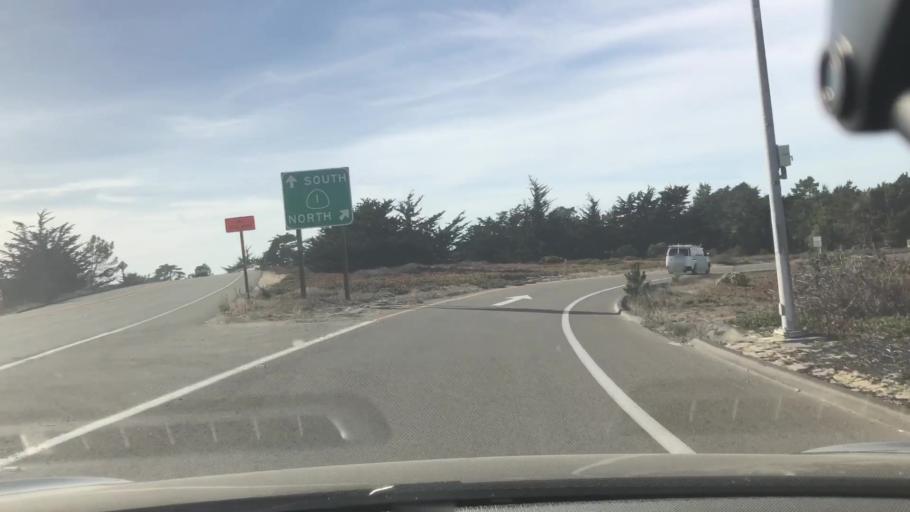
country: US
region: California
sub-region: Monterey County
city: Marina
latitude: 36.6478
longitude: -121.8134
